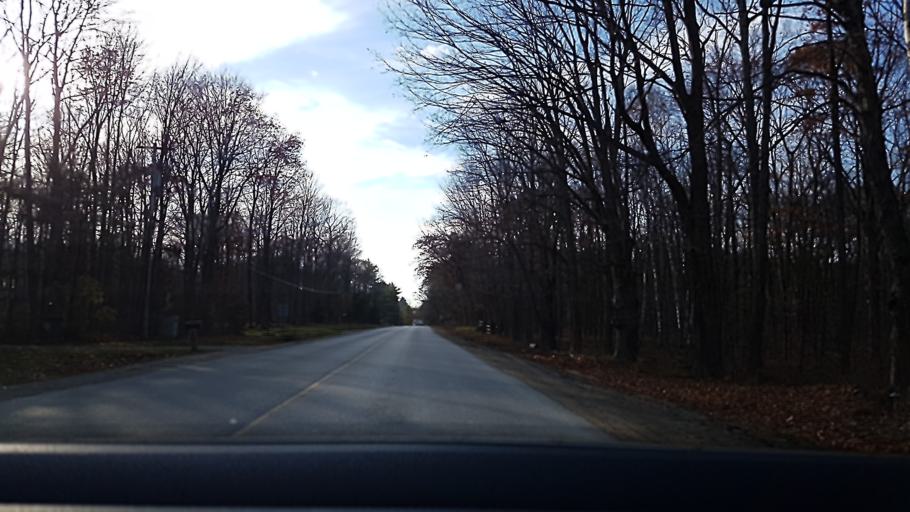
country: CA
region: Ontario
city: Barrie
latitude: 44.3925
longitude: -79.5477
